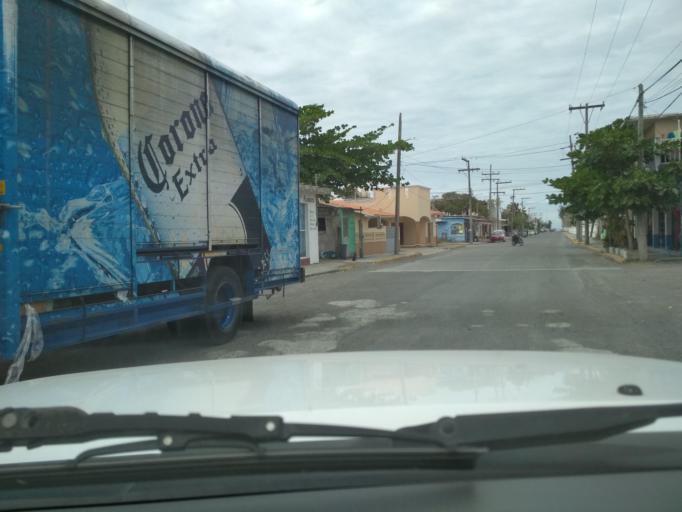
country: MX
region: Veracruz
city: Anton Lizardo
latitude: 19.0548
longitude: -95.9863
